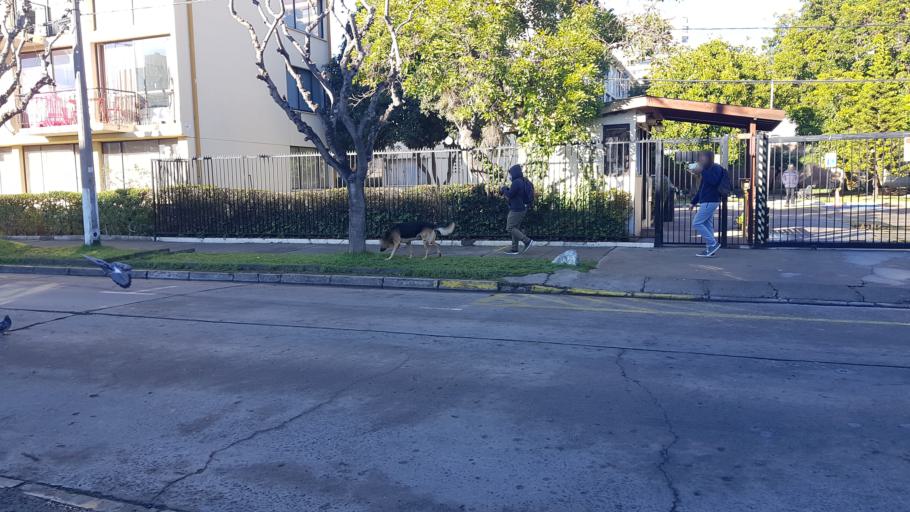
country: CL
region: Valparaiso
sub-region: Provincia de Valparaiso
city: Vina del Mar
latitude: -33.0139
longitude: -71.5517
